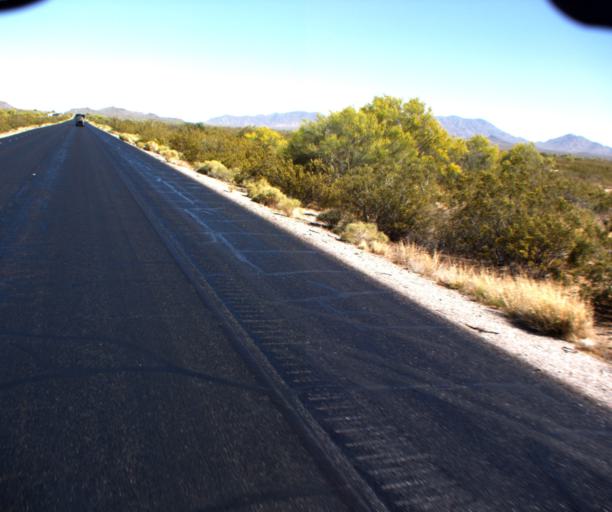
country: US
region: Arizona
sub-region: Pinal County
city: Maricopa
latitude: 32.8402
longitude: -112.2404
